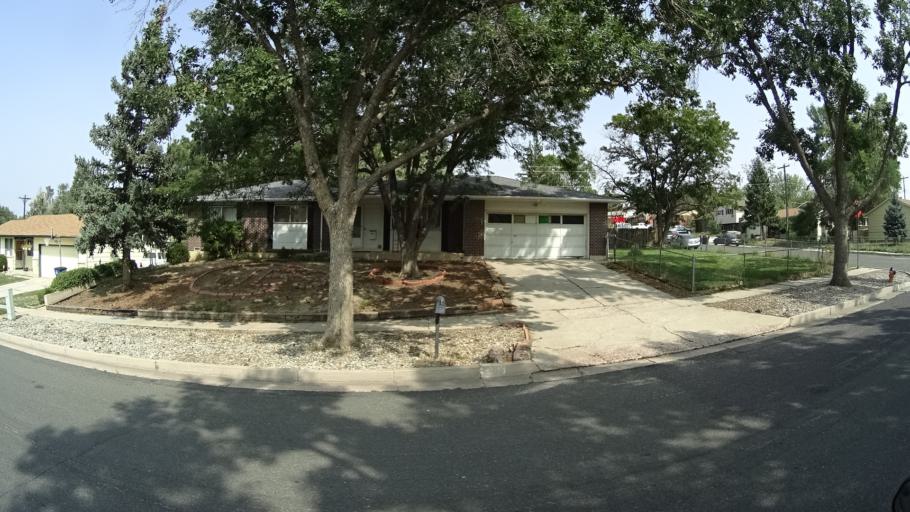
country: US
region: Colorado
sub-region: El Paso County
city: Stratmoor
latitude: 38.8071
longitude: -104.7722
